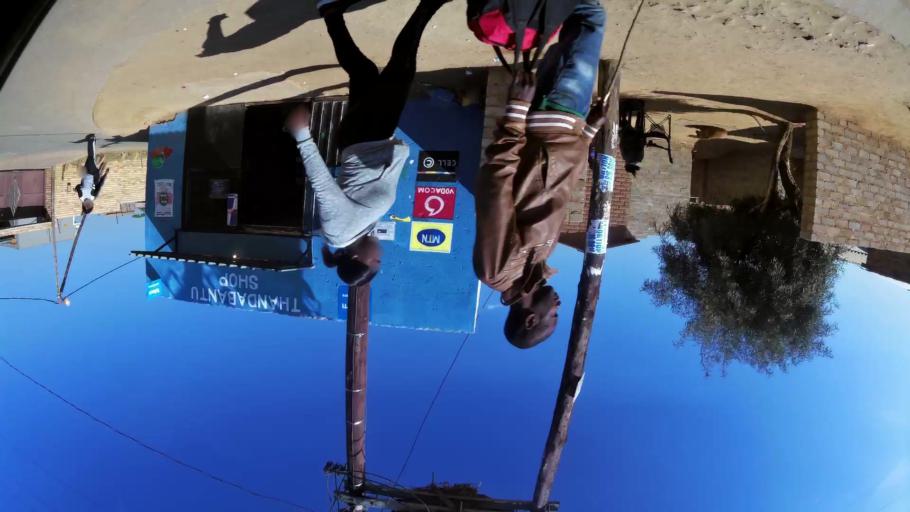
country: ZA
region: Gauteng
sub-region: West Rand District Municipality
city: Muldersdriseloop
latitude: -26.0262
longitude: 27.9281
